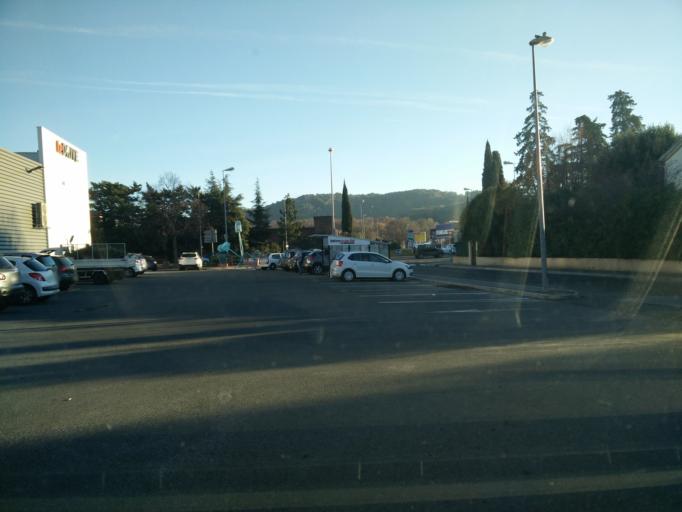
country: FR
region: Provence-Alpes-Cote d'Azur
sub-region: Departement du Var
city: Draguignan
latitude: 43.5325
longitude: 6.4491
